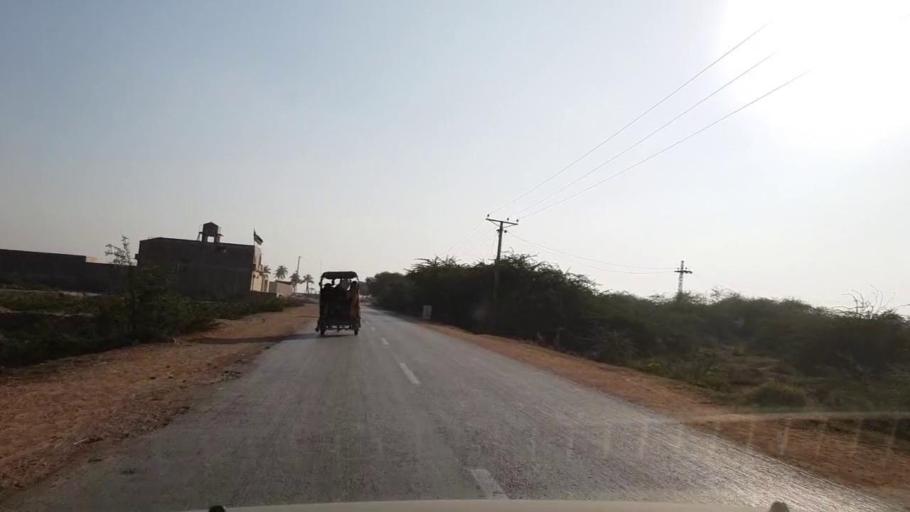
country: PK
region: Sindh
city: Bulri
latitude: 24.8571
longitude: 68.3286
